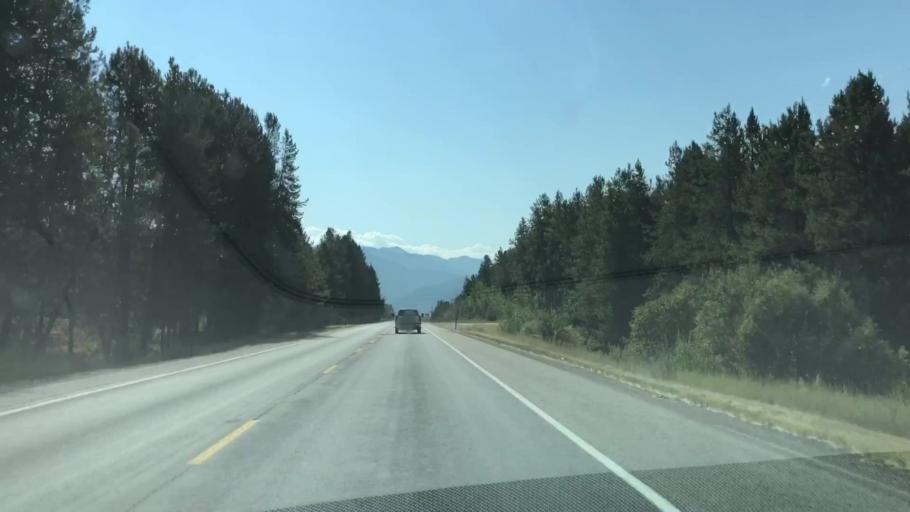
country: US
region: Wyoming
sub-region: Teton County
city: Hoback
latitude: 43.1982
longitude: -111.0419
